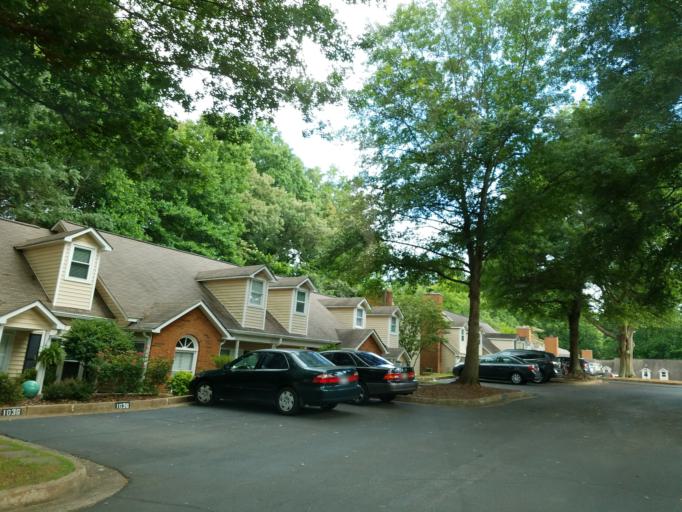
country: US
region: Georgia
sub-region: Fulton County
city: Roswell
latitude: 34.0341
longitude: -84.3576
